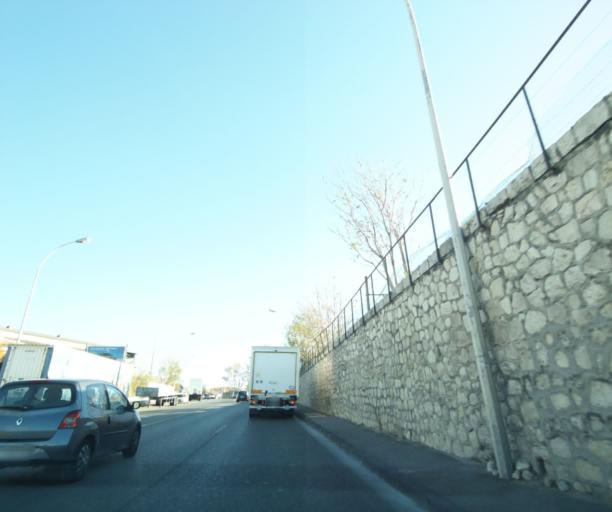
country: FR
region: Provence-Alpes-Cote d'Azur
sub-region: Departement des Bouches-du-Rhone
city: Marseille 14
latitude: 43.3471
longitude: 5.3637
